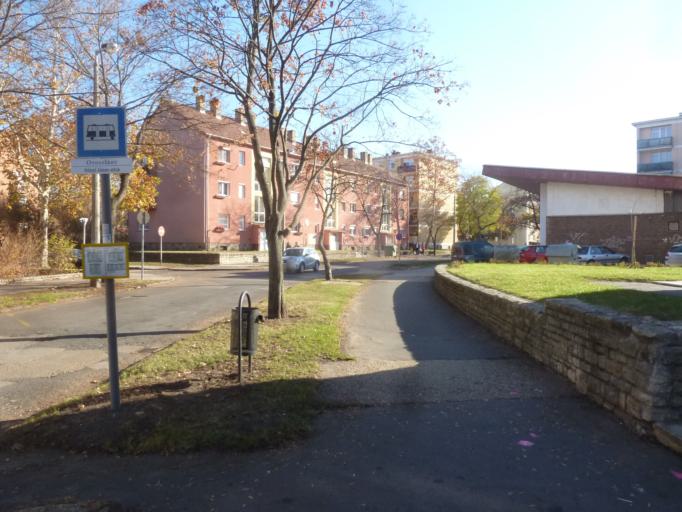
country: HU
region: Komarom-Esztergom
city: Oroszlany
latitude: 47.4864
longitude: 18.3118
